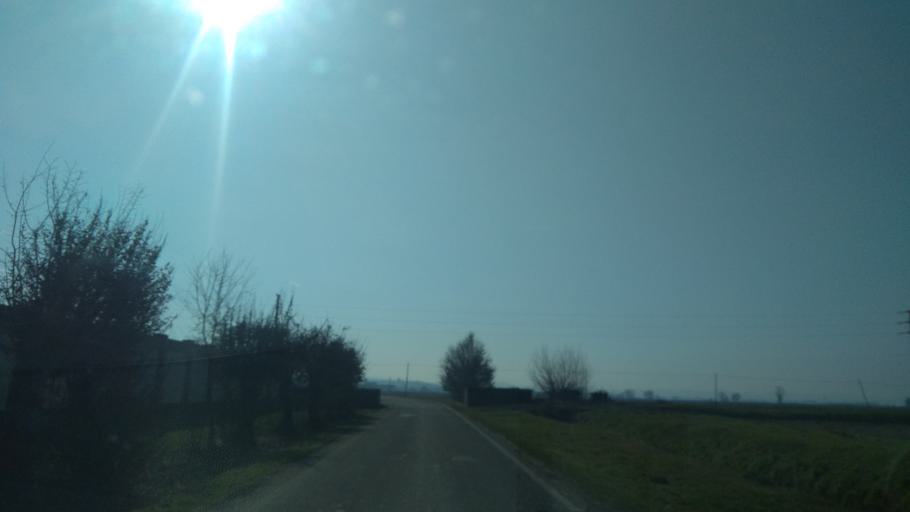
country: IT
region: Piedmont
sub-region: Provincia di Vercelli
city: Ronsecco
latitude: 45.2496
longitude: 8.2357
